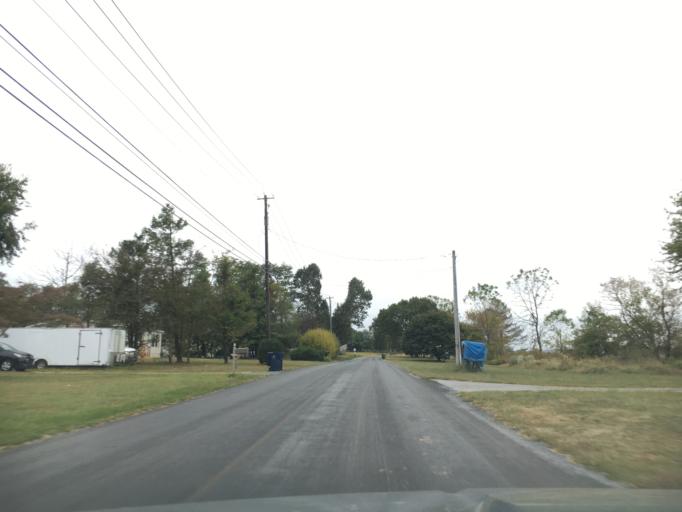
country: US
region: Pennsylvania
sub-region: Lancaster County
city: Christiana
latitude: 39.9384
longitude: -76.0289
